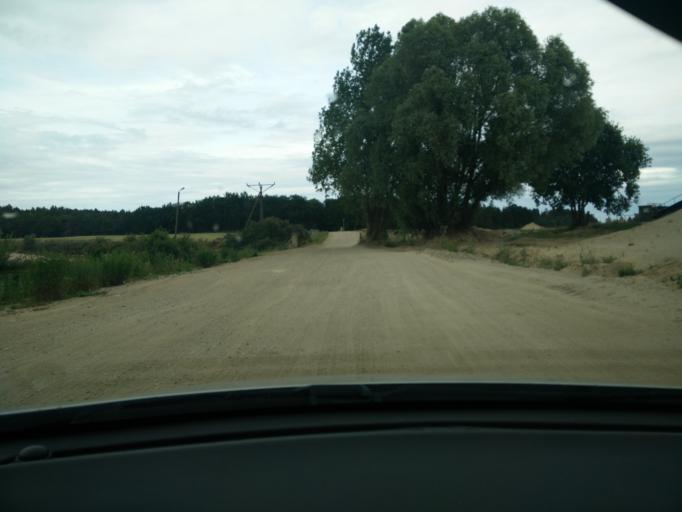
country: PL
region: Pomeranian Voivodeship
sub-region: Powiat pucki
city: Mrzezino
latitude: 54.6559
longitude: 18.4370
